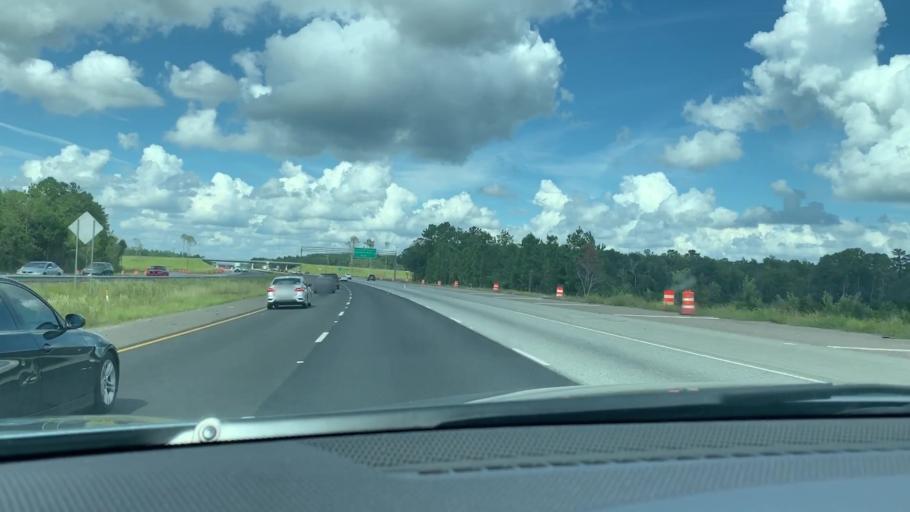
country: US
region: Georgia
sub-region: Camden County
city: Kingsland
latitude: 30.8410
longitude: -81.6698
